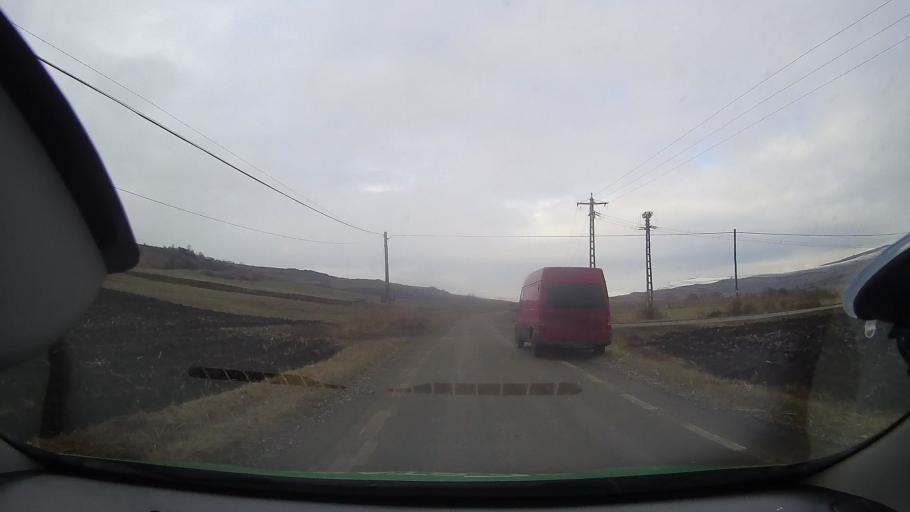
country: RO
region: Mures
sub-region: Comuna Bichis
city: Bichis
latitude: 46.3965
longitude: 24.0889
